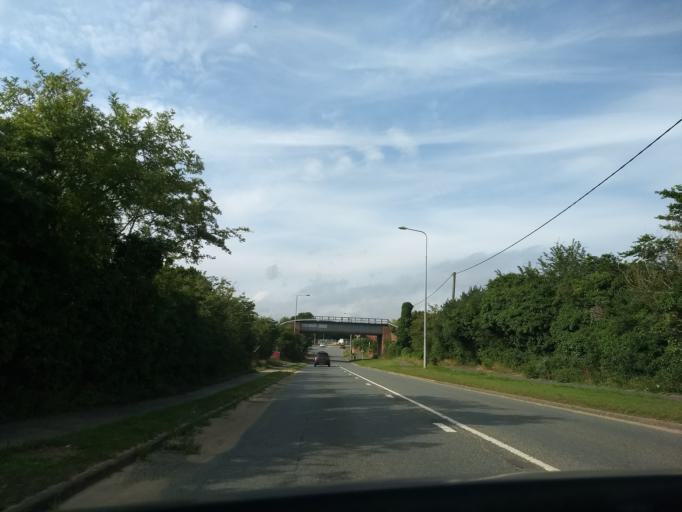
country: GB
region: England
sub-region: Suffolk
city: Woodbridge
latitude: 52.0802
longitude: 1.2873
